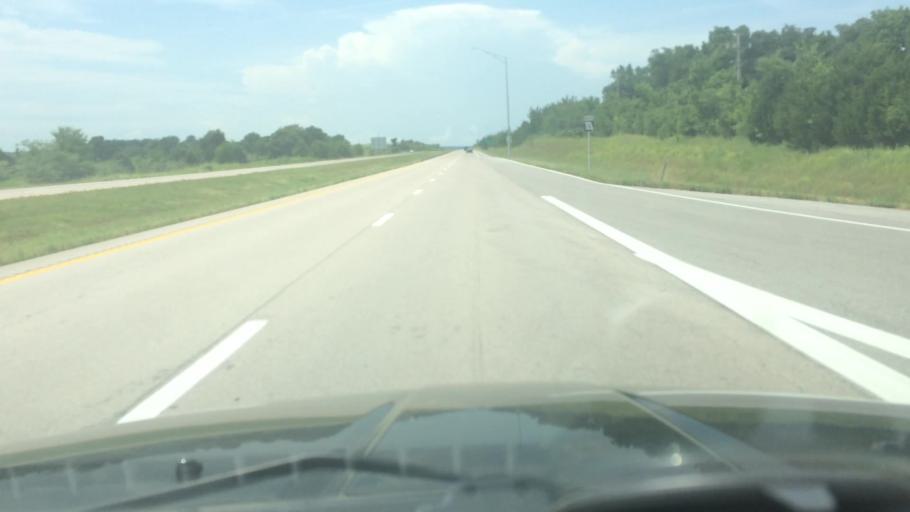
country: US
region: Missouri
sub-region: Polk County
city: Humansville
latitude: 37.7955
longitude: -93.5898
